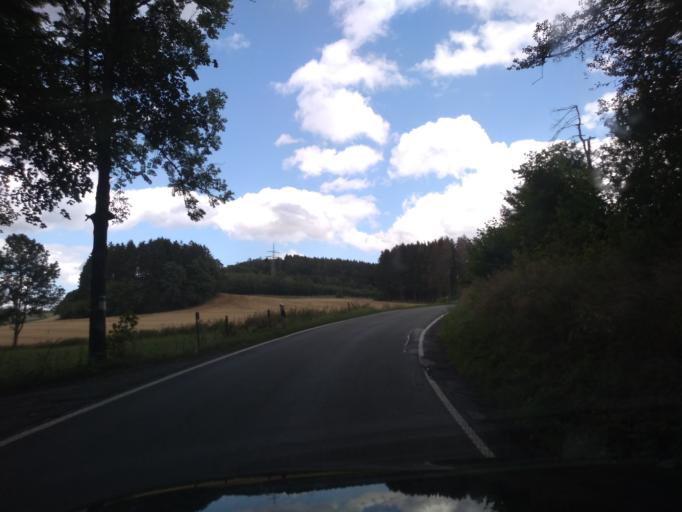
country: DE
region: North Rhine-Westphalia
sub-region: Regierungsbezirk Arnsberg
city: Luedenscheid
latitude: 51.2337
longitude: 7.5880
